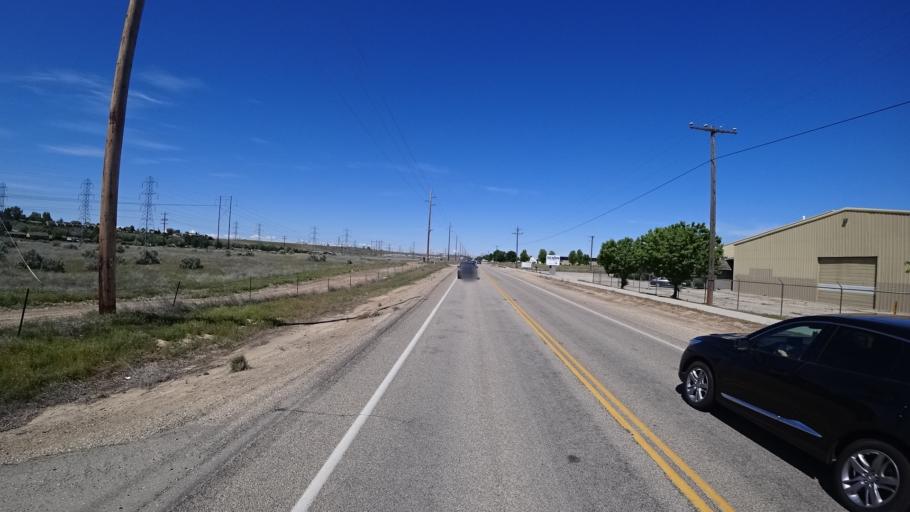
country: US
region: Idaho
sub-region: Ada County
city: Boise
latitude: 43.5599
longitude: -116.1437
